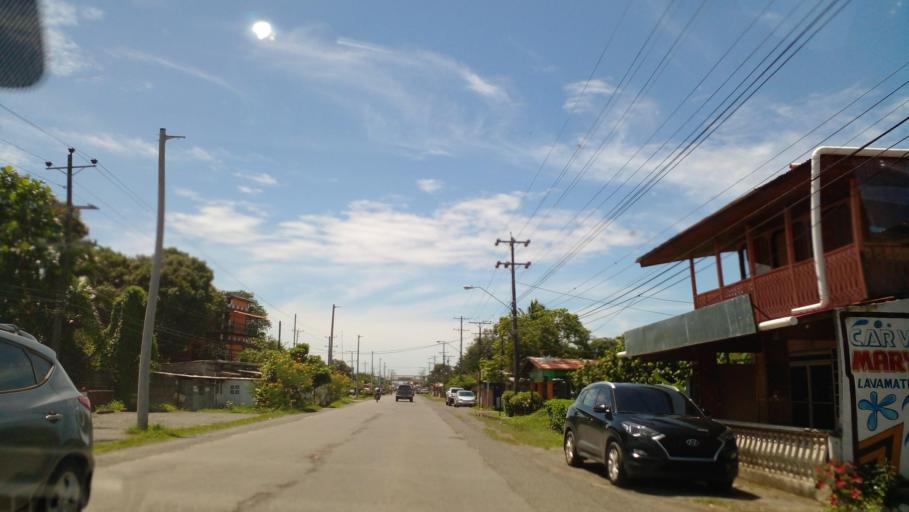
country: PA
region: Bocas del Toro
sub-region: Distrito de Changuinola
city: Changuinola
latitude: 9.4422
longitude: -82.5189
